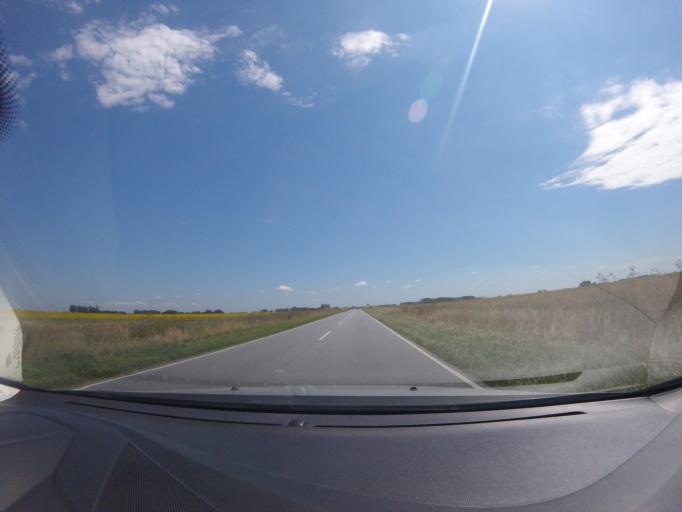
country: AR
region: Buenos Aires
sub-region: Partido de Tandil
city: Tandil
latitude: -37.1327
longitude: -58.9997
